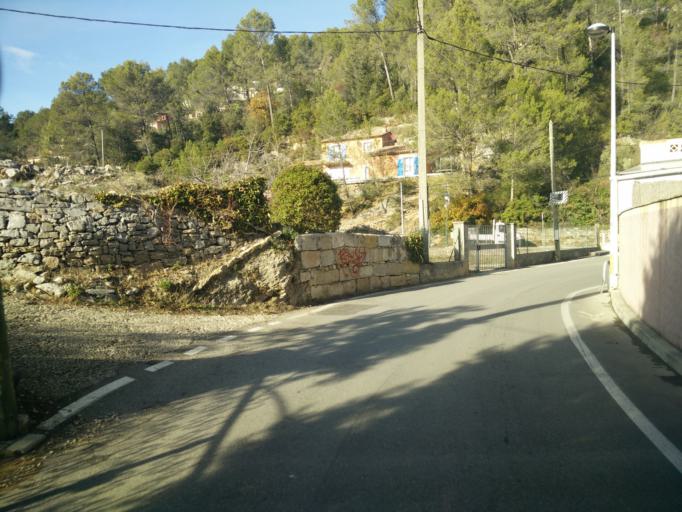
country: FR
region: Provence-Alpes-Cote d'Azur
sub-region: Departement du Var
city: Sollies-Toucas
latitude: 43.2024
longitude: 6.0193
